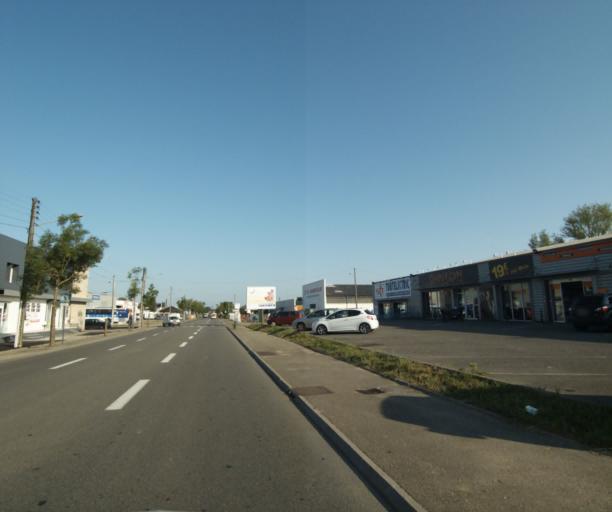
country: FR
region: Midi-Pyrenees
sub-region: Departement du Tarn-et-Garonne
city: Montauban
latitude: 44.0342
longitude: 1.3732
